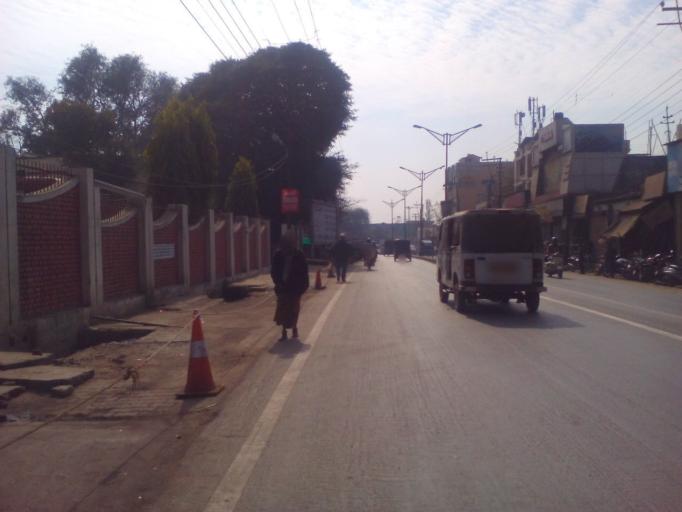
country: IN
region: Uttarakhand
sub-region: Dehradun
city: Dehradun
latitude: 30.3192
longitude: 78.0401
